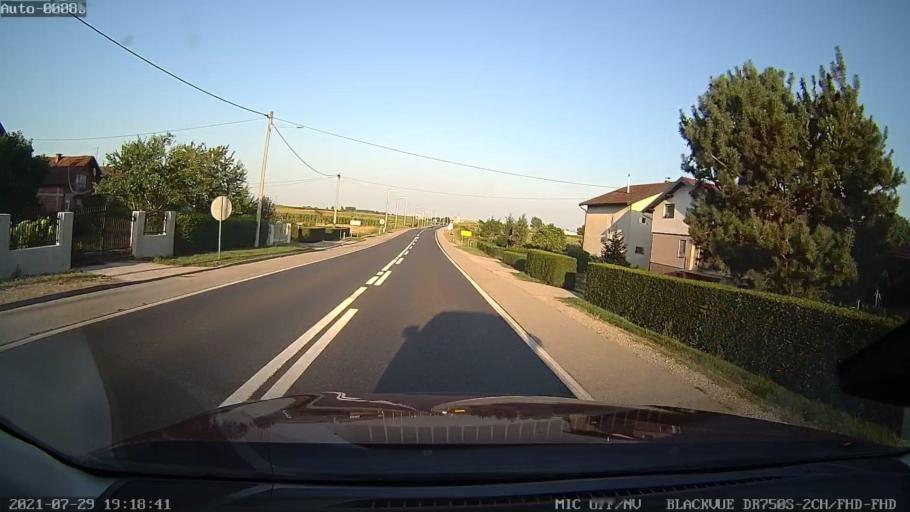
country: HR
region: Varazdinska
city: Ludbreg
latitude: 46.2596
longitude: 16.5889
